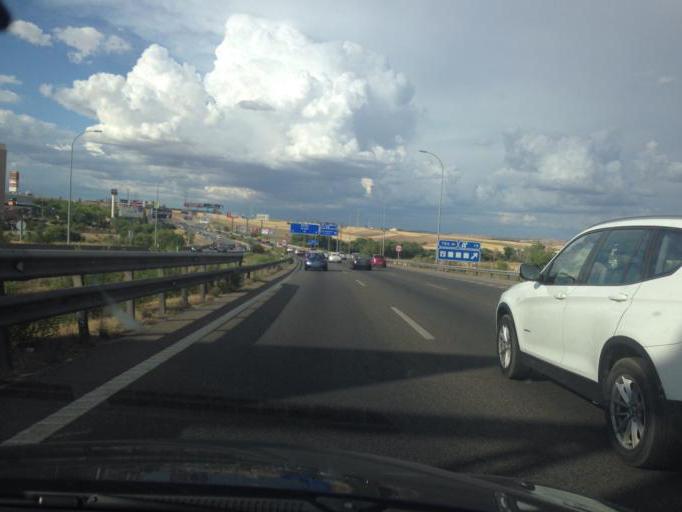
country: ES
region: Madrid
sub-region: Provincia de Madrid
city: San Sebastian de los Reyes
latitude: 40.5354
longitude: -3.6132
